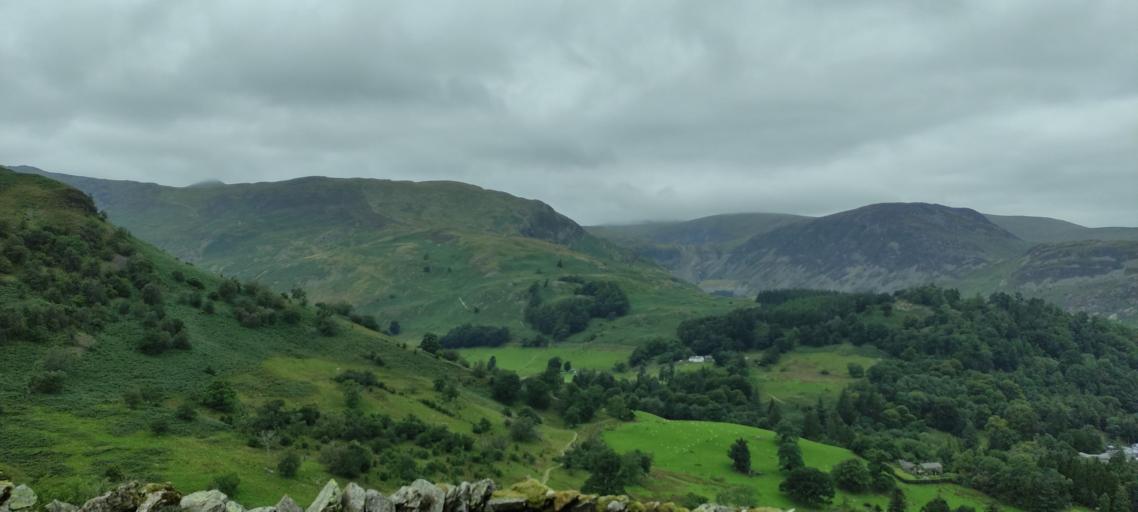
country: GB
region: England
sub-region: Cumbria
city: Ambleside
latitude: 54.5296
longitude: -2.9399
